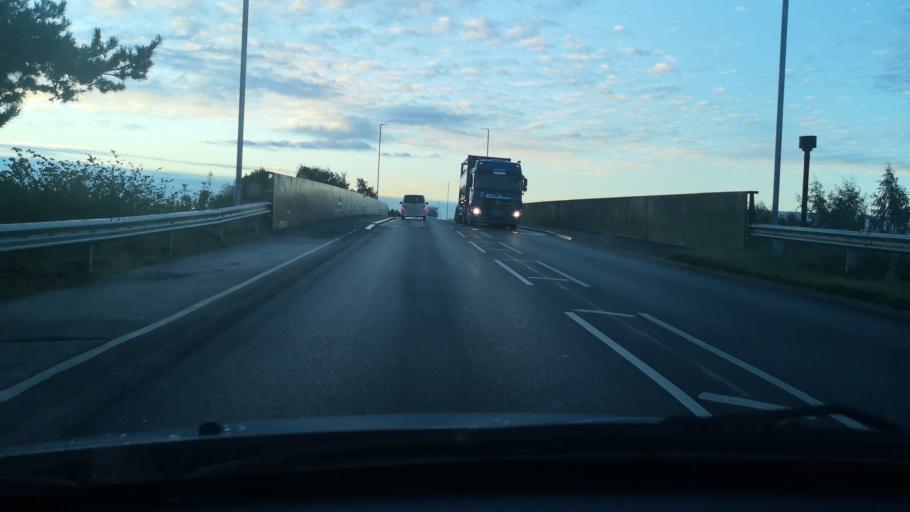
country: GB
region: England
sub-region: East Riding of Yorkshire
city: Airmyn
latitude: 53.7003
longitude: -0.8873
